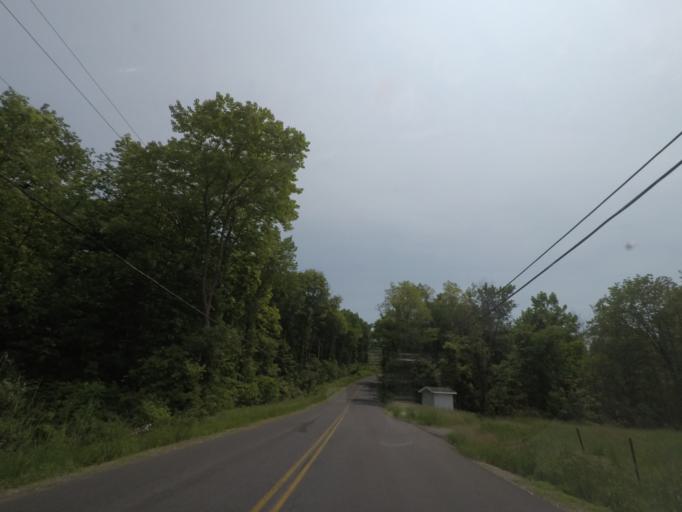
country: US
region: New York
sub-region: Rensselaer County
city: Castleton-on-Hudson
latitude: 42.5177
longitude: -73.7069
